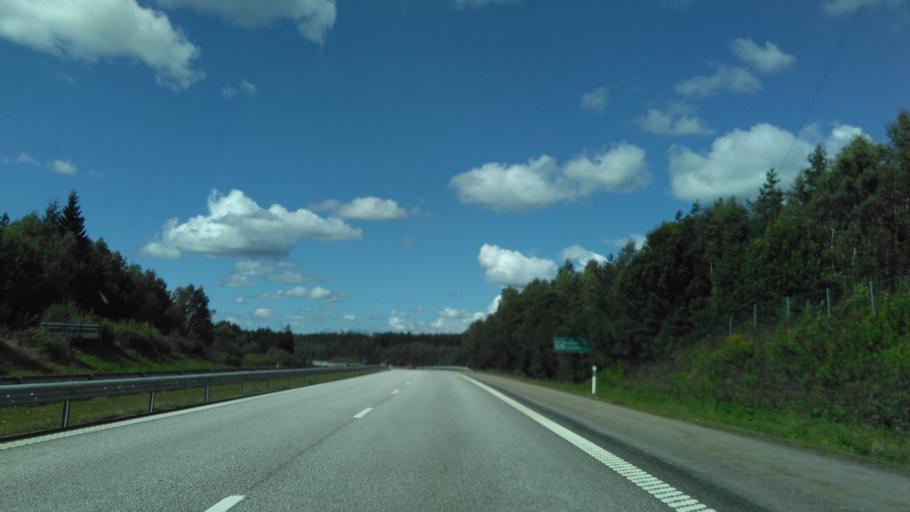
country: SE
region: Vaestra Goetaland
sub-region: Harryda Kommun
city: Ravlanda
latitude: 57.6704
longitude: 12.5196
